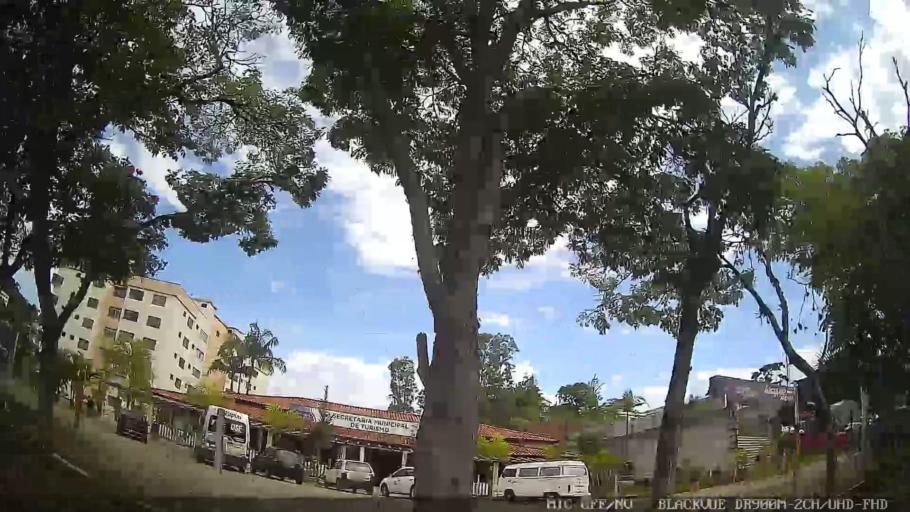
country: BR
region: Sao Paulo
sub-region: Serra Negra
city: Serra Negra
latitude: -22.6067
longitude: -46.7067
